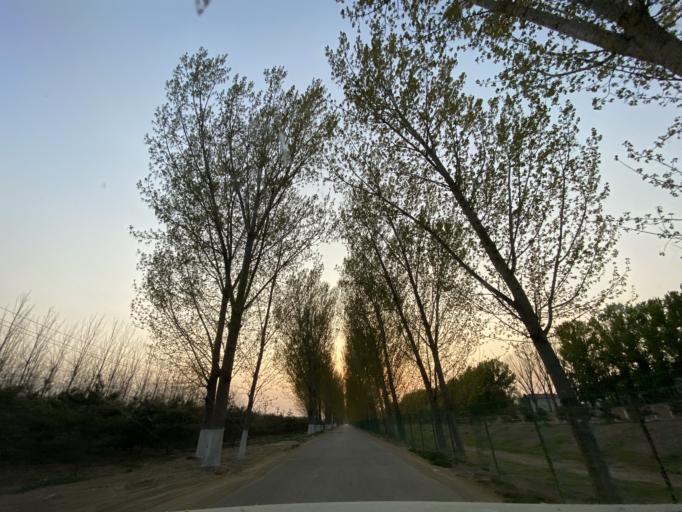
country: CN
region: Beijing
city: Weishanzhuang
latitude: 39.6064
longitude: 116.4212
